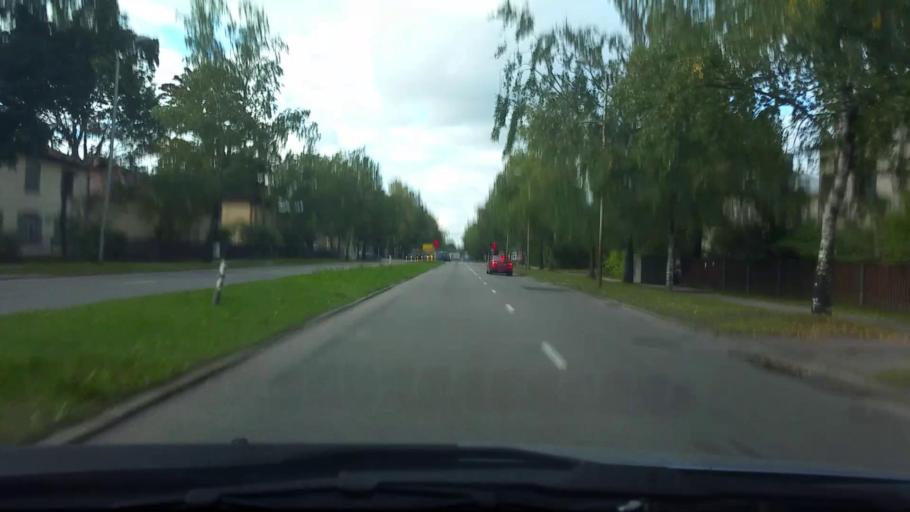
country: LV
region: Riga
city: Jaunciems
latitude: 56.9747
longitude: 24.1896
